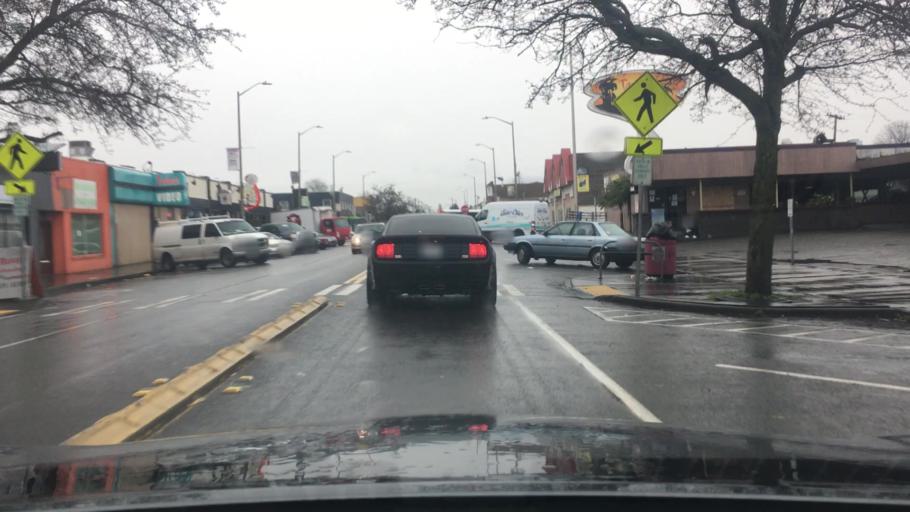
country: US
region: Washington
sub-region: King County
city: White Center
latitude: 47.5147
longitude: -122.3551
